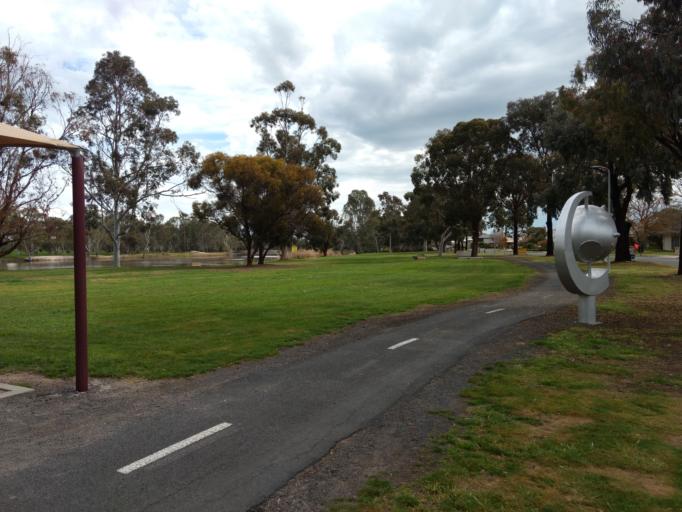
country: AU
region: Victoria
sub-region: Horsham
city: Horsham
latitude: -36.7250
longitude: 142.1896
